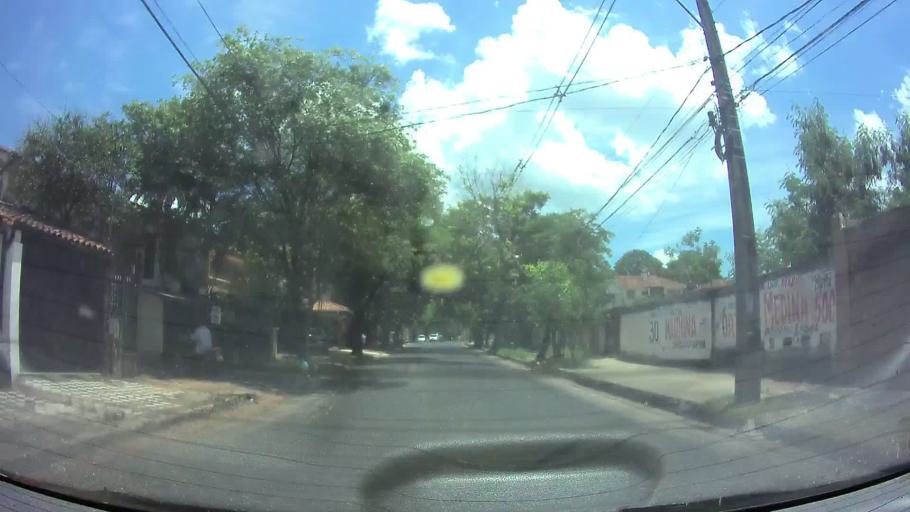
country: PY
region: Asuncion
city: Asuncion
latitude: -25.3009
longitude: -57.6002
